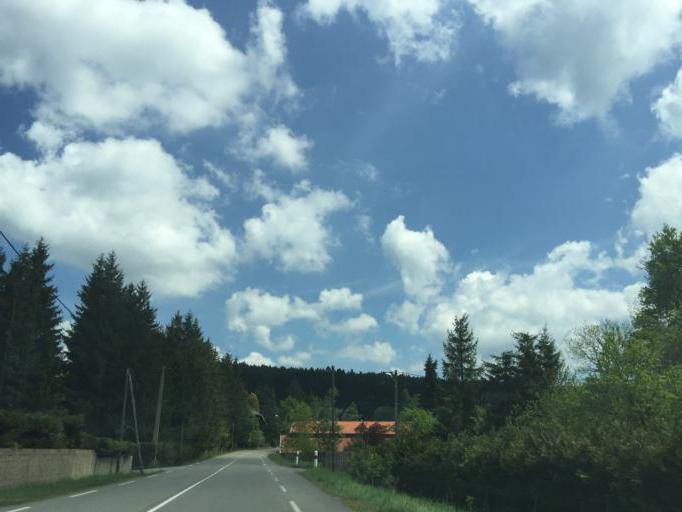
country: FR
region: Rhone-Alpes
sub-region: Departement de la Loire
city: Saint-Genest-Malifaux
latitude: 45.3498
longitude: 4.4775
